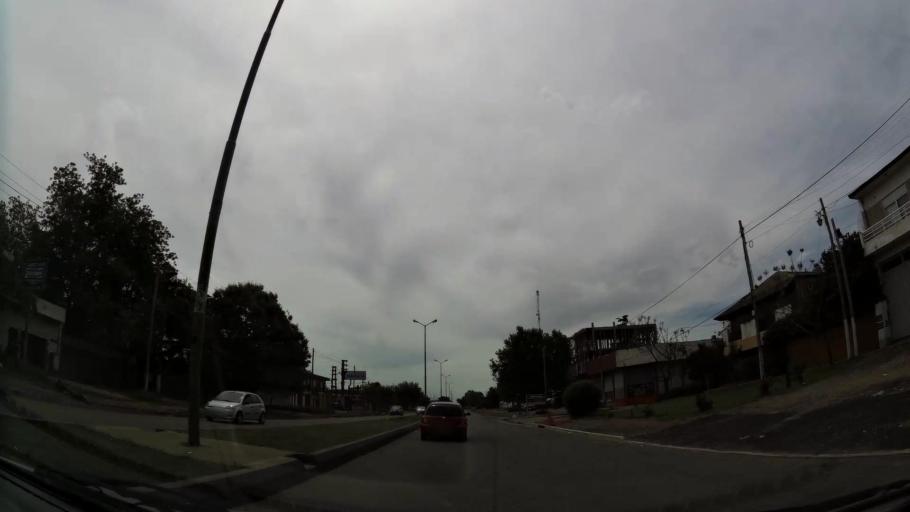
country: AR
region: Buenos Aires
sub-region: Partido de Quilmes
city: Quilmes
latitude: -34.7724
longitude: -58.2822
